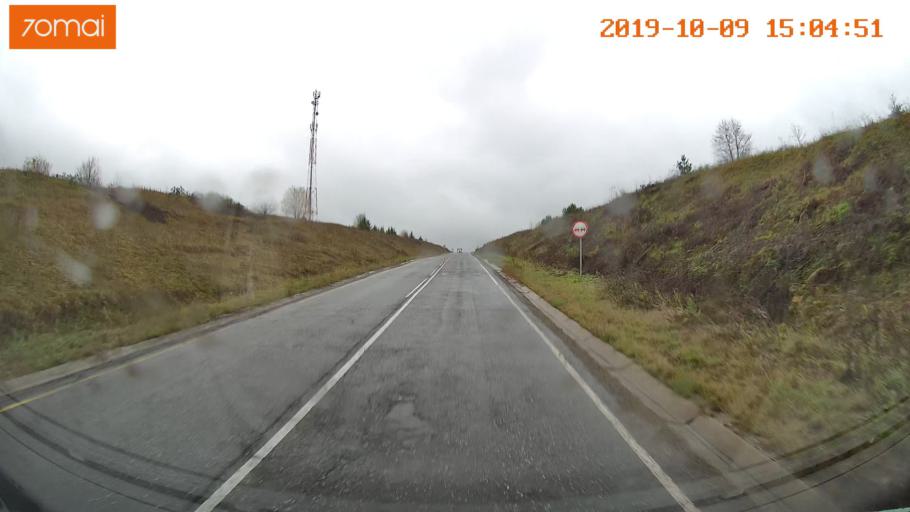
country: RU
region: Kostroma
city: Chistyye Bory
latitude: 58.2537
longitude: 41.6641
